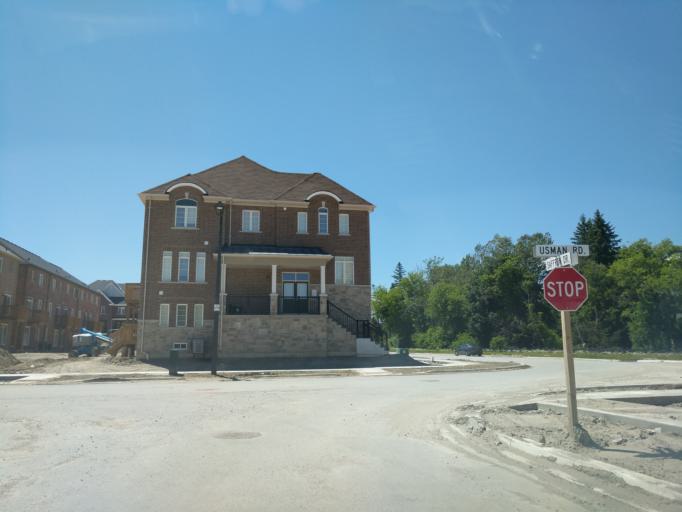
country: CA
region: Ontario
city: Ajax
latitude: 43.8552
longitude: -79.0758
